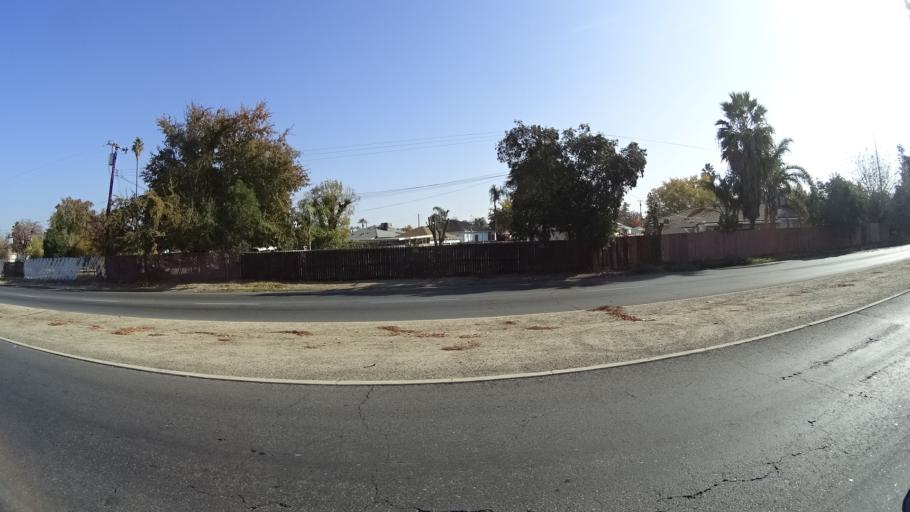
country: US
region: California
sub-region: Kern County
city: Bakersfield
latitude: 35.3486
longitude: -119.0213
